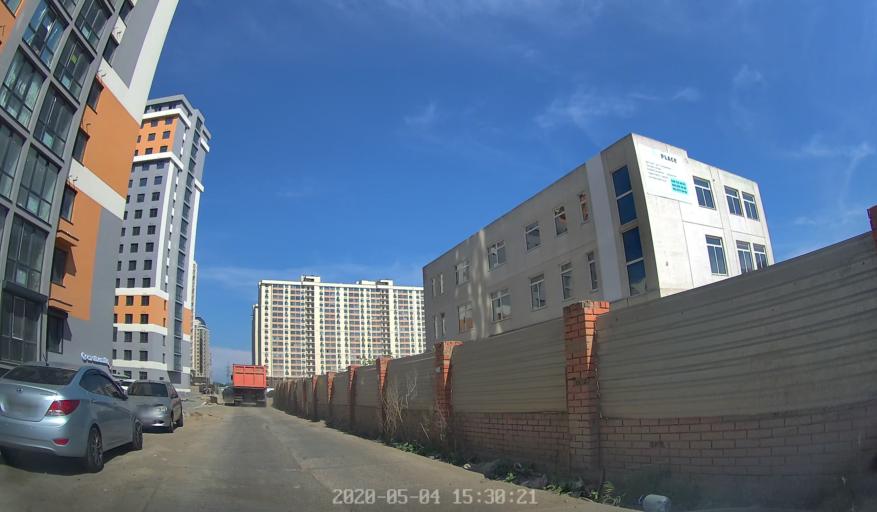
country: TR
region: Kirklareli
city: Sergen
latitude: 41.7422
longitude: 27.6343
